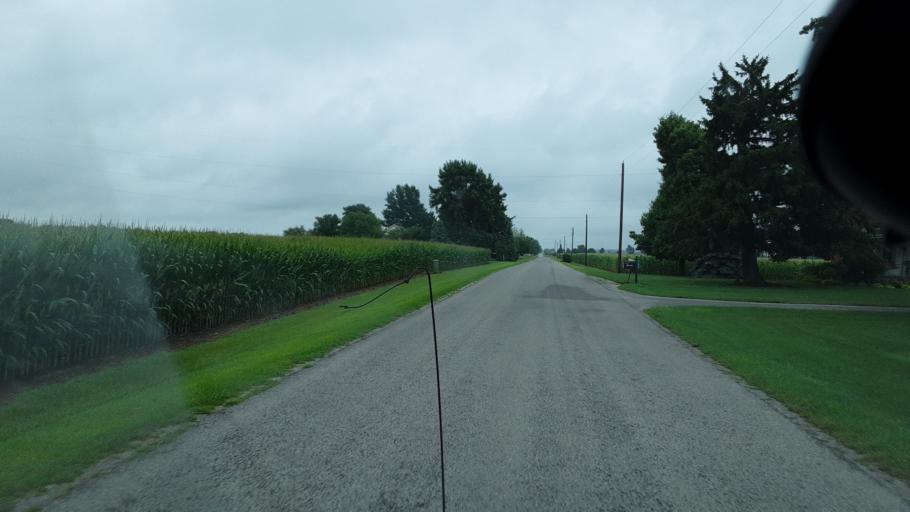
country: US
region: Indiana
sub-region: Wells County
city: Ossian
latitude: 40.9221
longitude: -85.1097
